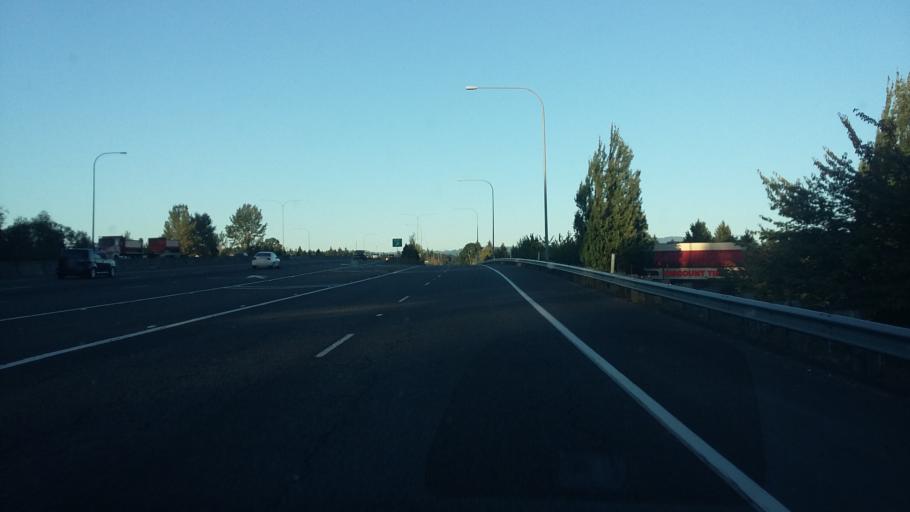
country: US
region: Washington
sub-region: Clark County
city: Walnut Grove
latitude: 45.6521
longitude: -122.5917
